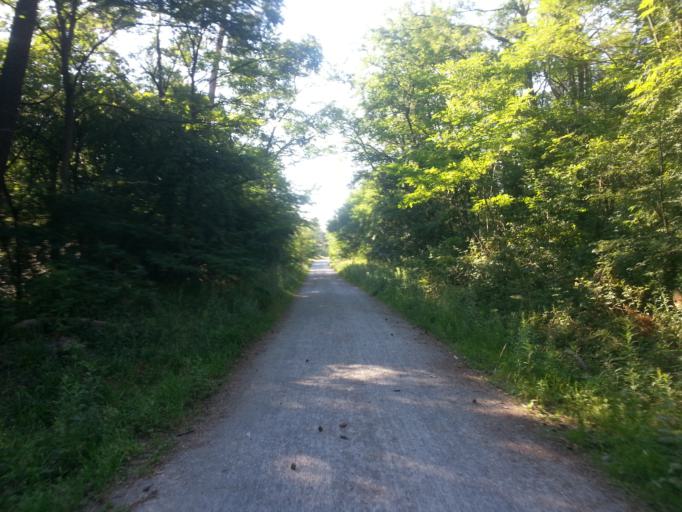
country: DE
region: Hesse
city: Viernheim
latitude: 49.5469
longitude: 8.5454
